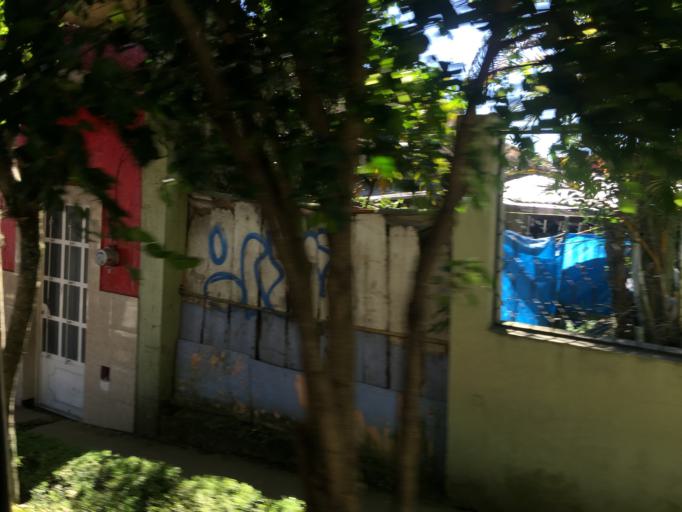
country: MX
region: Veracruz
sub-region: Xalapa
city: Xalapa de Enriquez
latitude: 19.5381
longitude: -96.9166
